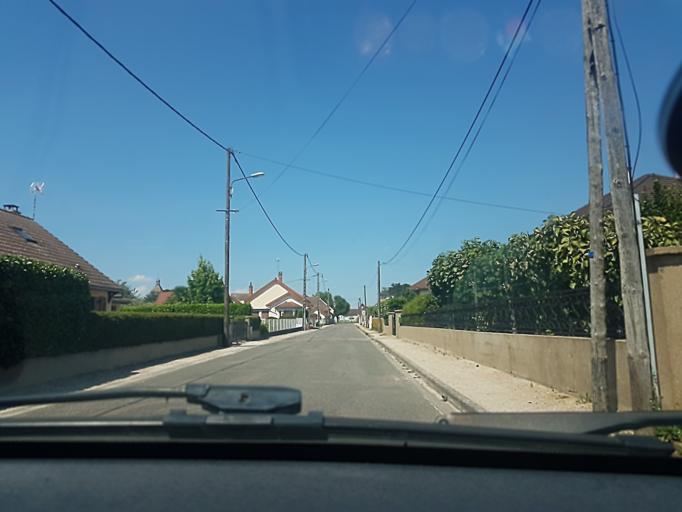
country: FR
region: Bourgogne
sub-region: Departement de Saone-et-Loire
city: Saint-Marcel
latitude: 46.7717
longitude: 4.8891
